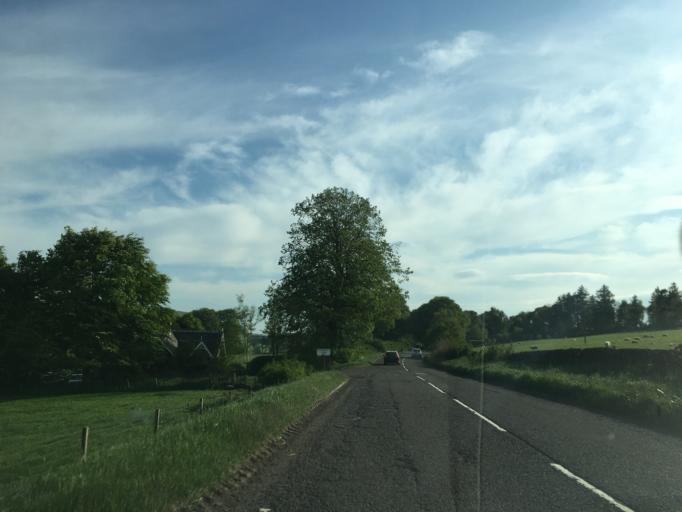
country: GB
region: Scotland
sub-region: The Scottish Borders
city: West Linton
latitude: 55.7105
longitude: -3.3510
